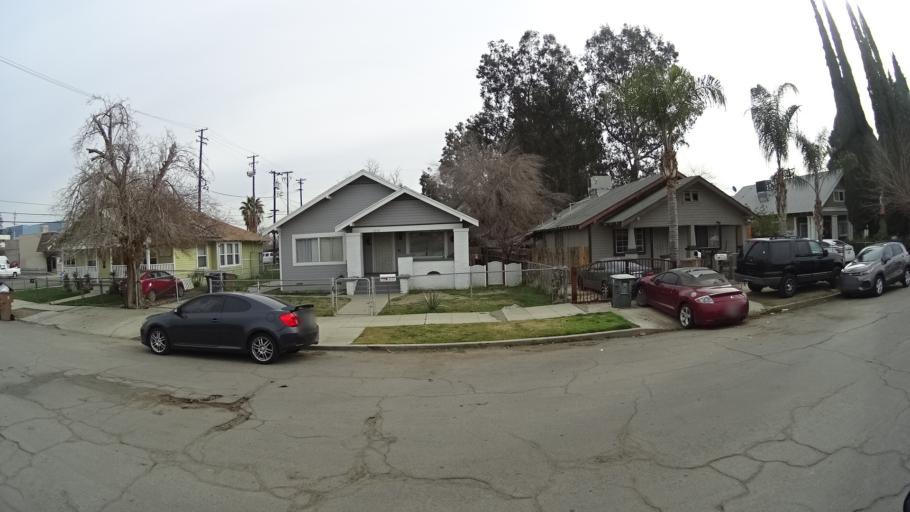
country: US
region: California
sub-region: Kern County
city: Bakersfield
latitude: 35.3701
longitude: -119.0153
